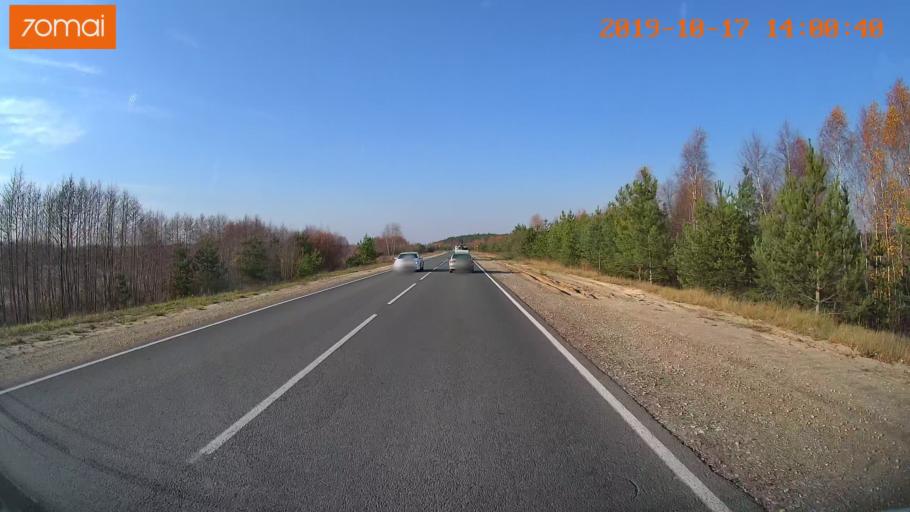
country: RU
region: Rjazan
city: Spas-Klepiki
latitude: 55.1475
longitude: 40.1765
